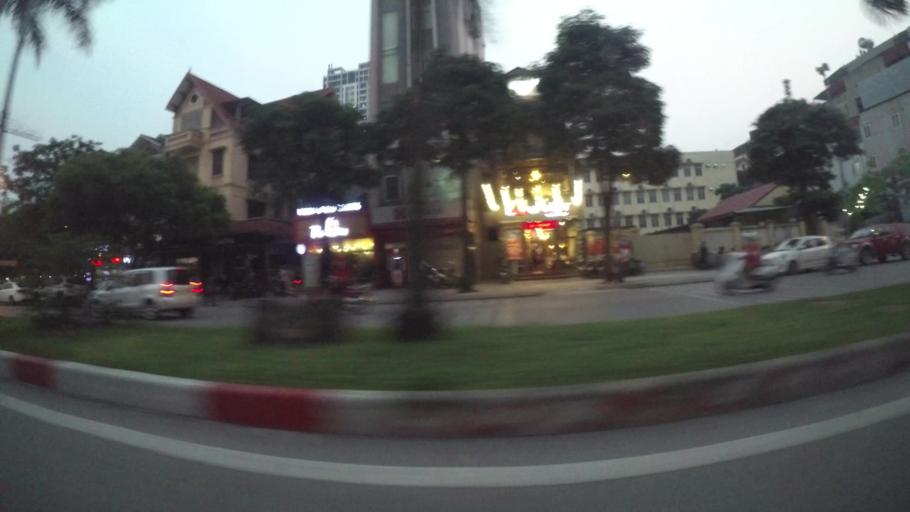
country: VN
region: Ha Noi
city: Ha Dong
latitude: 20.9761
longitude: 105.7893
